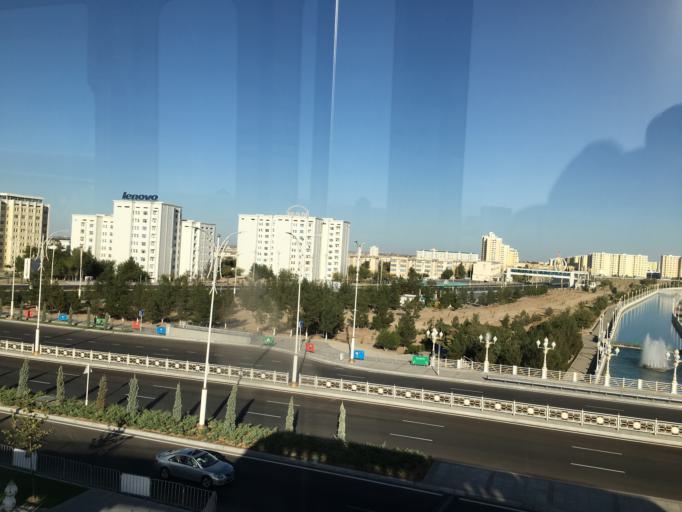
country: TM
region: Ahal
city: Ashgabat
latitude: 37.9110
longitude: 58.3804
